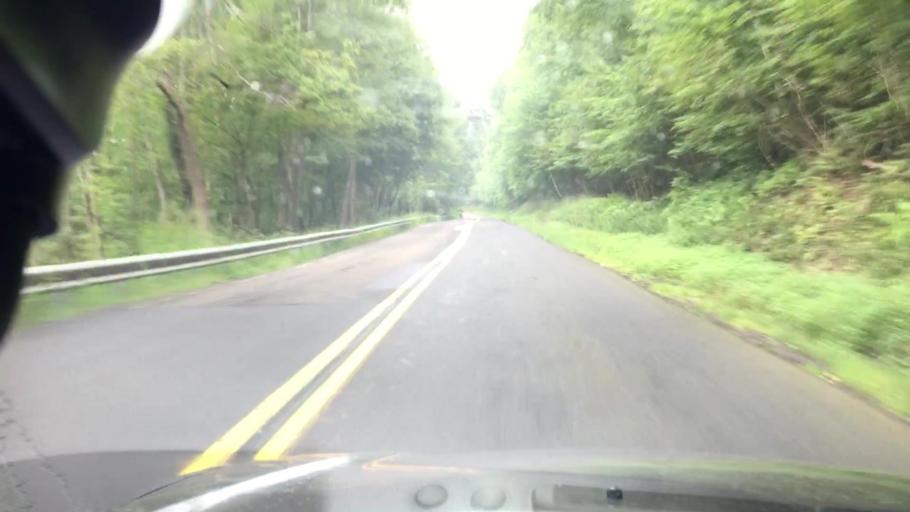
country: US
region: Pennsylvania
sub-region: Luzerne County
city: Harleigh
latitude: 40.9996
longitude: -75.9945
